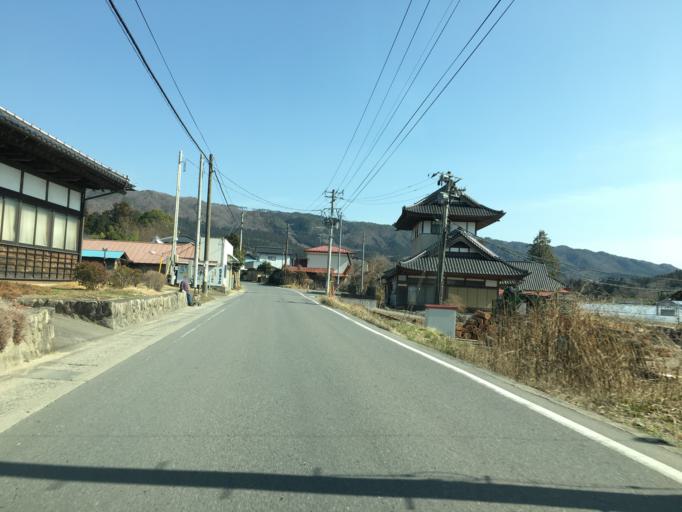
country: JP
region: Ibaraki
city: Daigo
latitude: 36.8391
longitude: 140.4413
